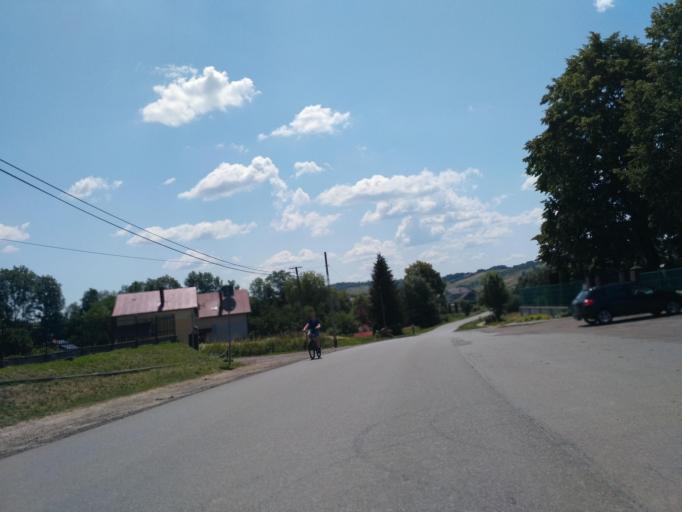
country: PL
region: Subcarpathian Voivodeship
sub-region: Powiat sanocki
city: Niebieszczany
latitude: 49.5071
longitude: 22.1550
